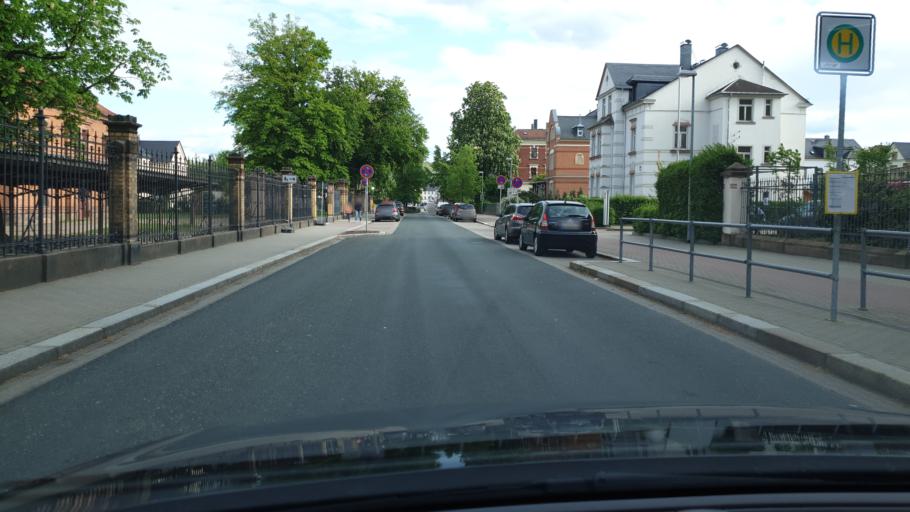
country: DE
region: Saxony
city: Rochlitz
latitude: 51.0492
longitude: 12.7974
